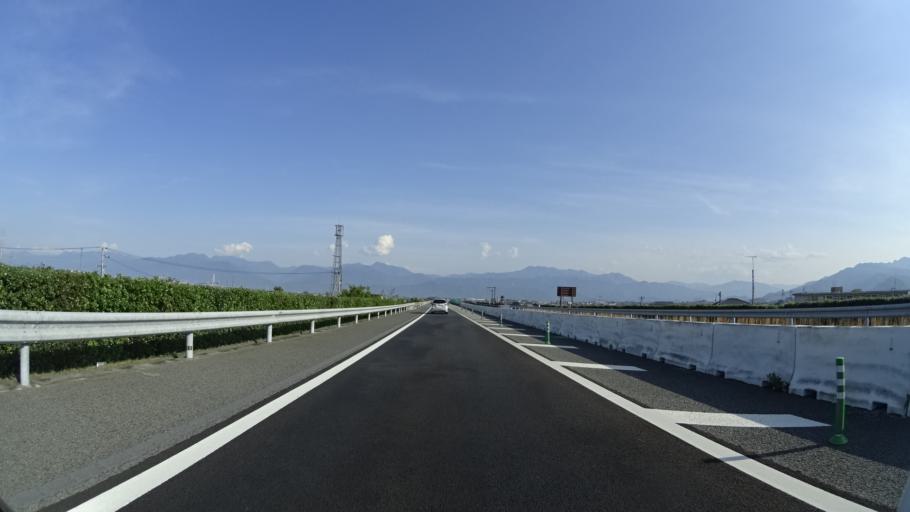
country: JP
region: Ehime
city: Saijo
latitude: 33.9655
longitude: 133.0627
